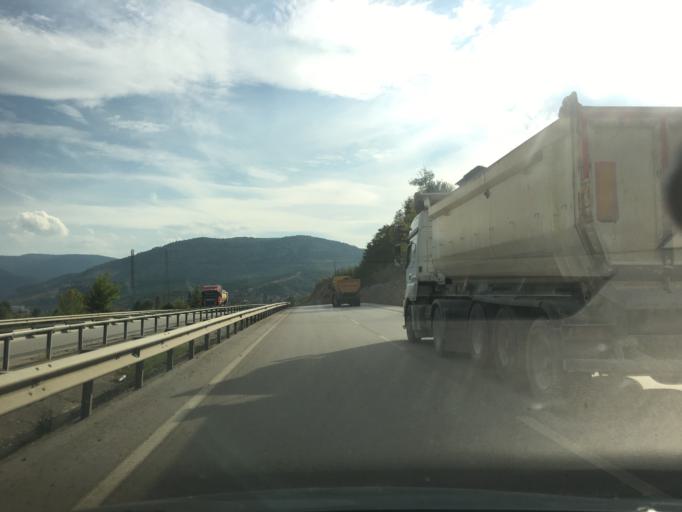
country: TR
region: Karabuk
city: Karabuk
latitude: 41.1127
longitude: 32.6701
